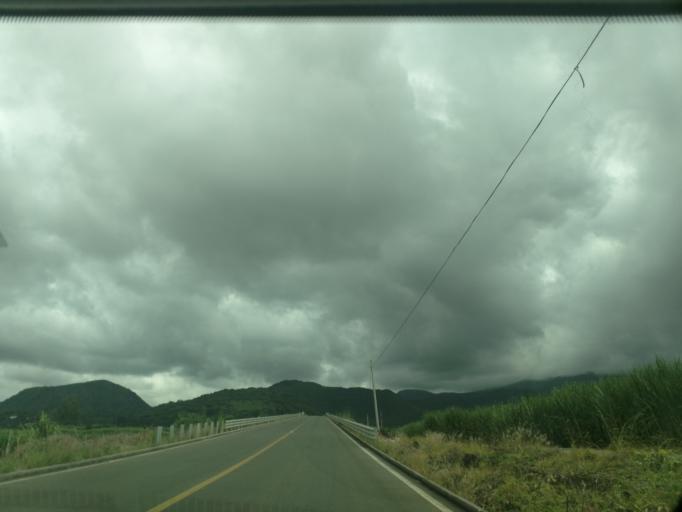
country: MX
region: Nayarit
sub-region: Tepic
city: La Corregidora
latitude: 21.4544
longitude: -104.8061
